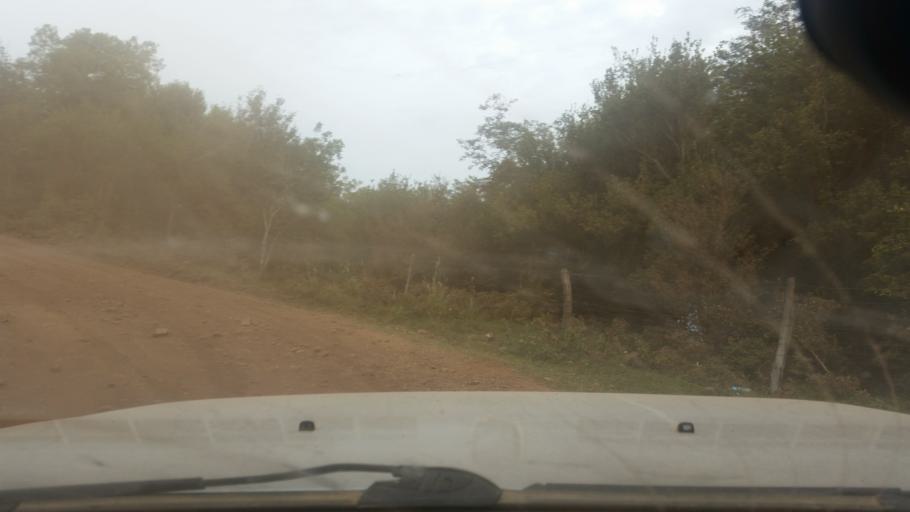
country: PY
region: Guaira
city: Independencia
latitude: -25.8179
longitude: -56.2770
